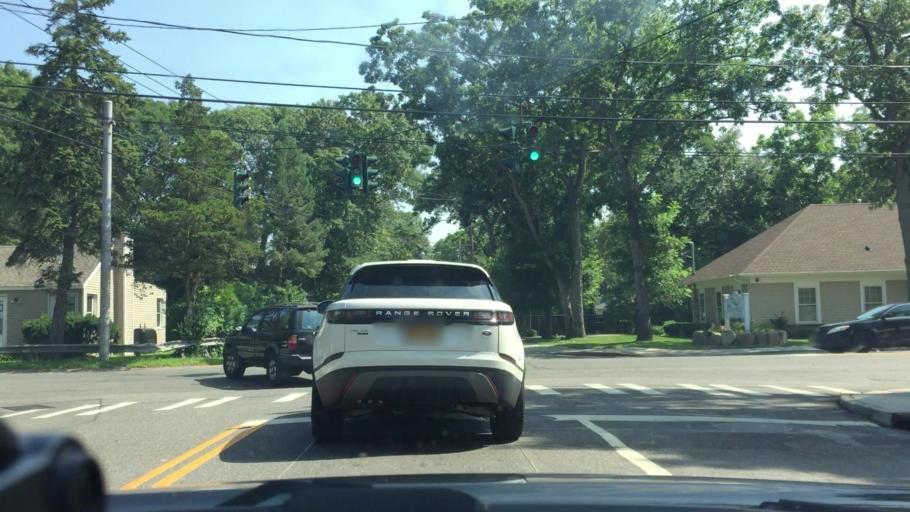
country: US
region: New York
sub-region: Suffolk County
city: Port Jefferson Station
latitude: 40.9326
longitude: -73.0454
